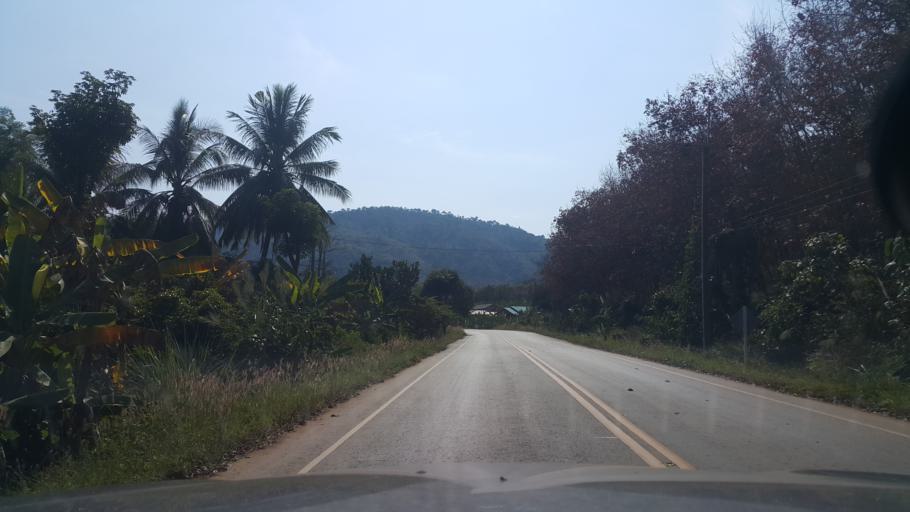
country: TH
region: Loei
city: Pak Chom
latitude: 18.0986
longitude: 102.0282
